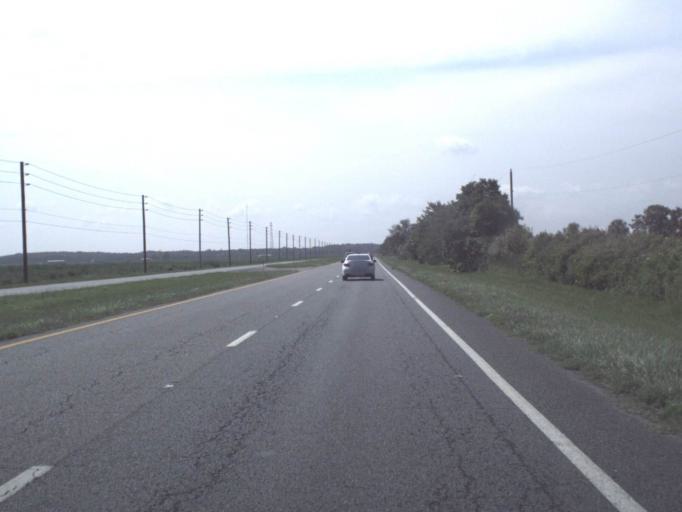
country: US
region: Florida
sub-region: Nassau County
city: Callahan
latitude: 30.6261
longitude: -81.8495
